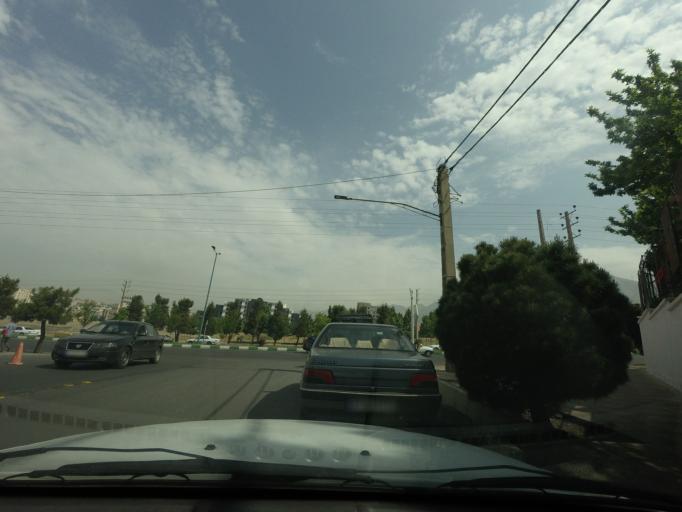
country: IR
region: Alborz
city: Karaj
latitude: 35.8423
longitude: 50.9956
